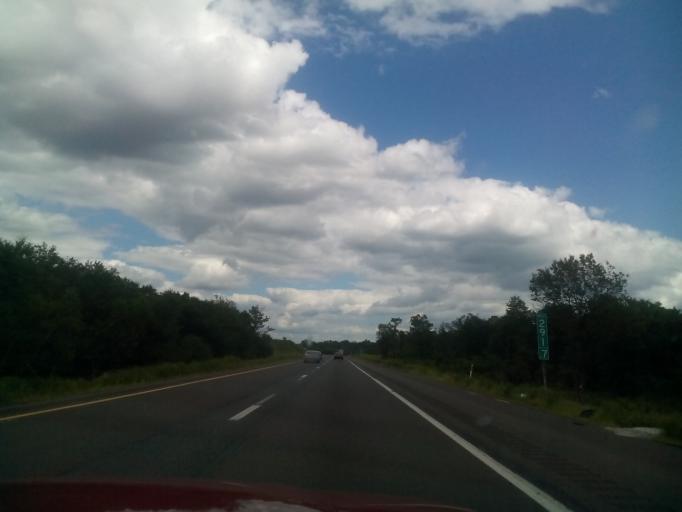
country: US
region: Pennsylvania
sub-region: Monroe County
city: Emerald Lakes
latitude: 41.0713
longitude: -75.4258
